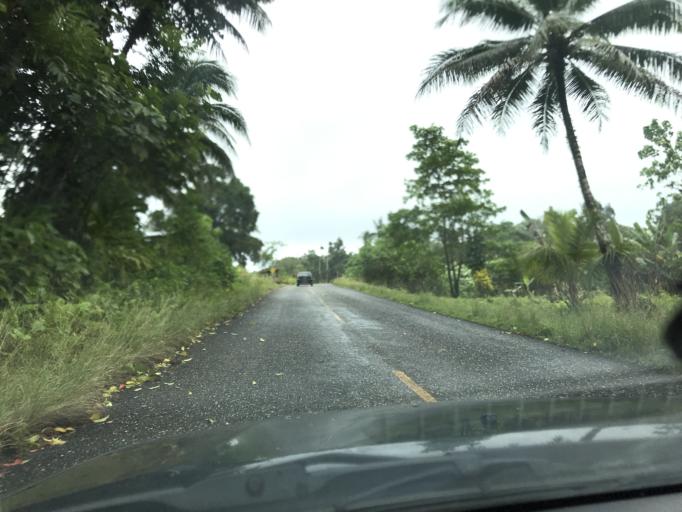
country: SB
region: Western Province
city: Gizo
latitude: -8.2466
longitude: 157.2354
